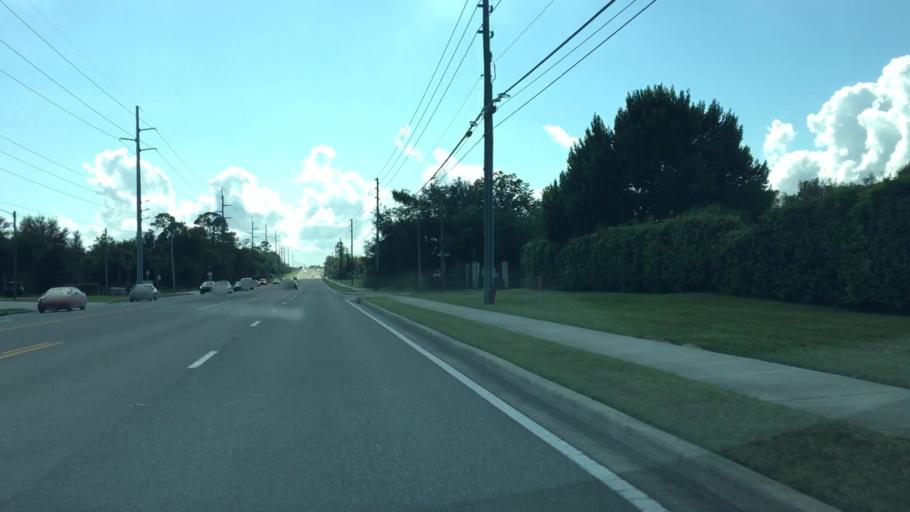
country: US
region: Florida
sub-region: Volusia County
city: Deltona
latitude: 28.8948
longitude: -81.2835
